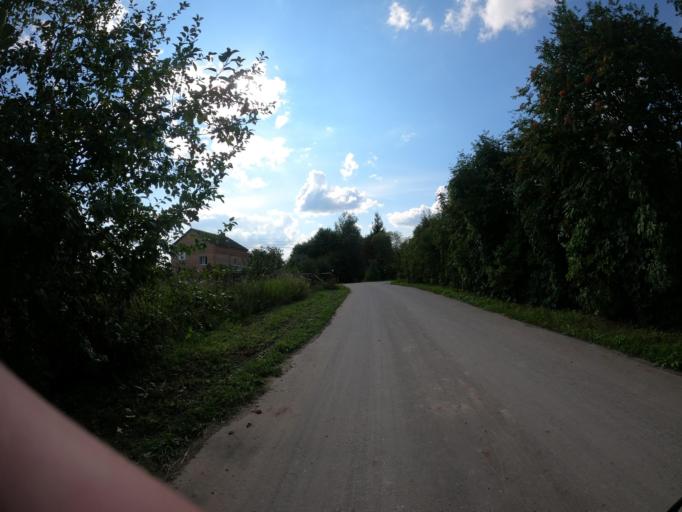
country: RU
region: Moskovskaya
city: Troitskoye
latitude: 55.2410
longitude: 38.4866
